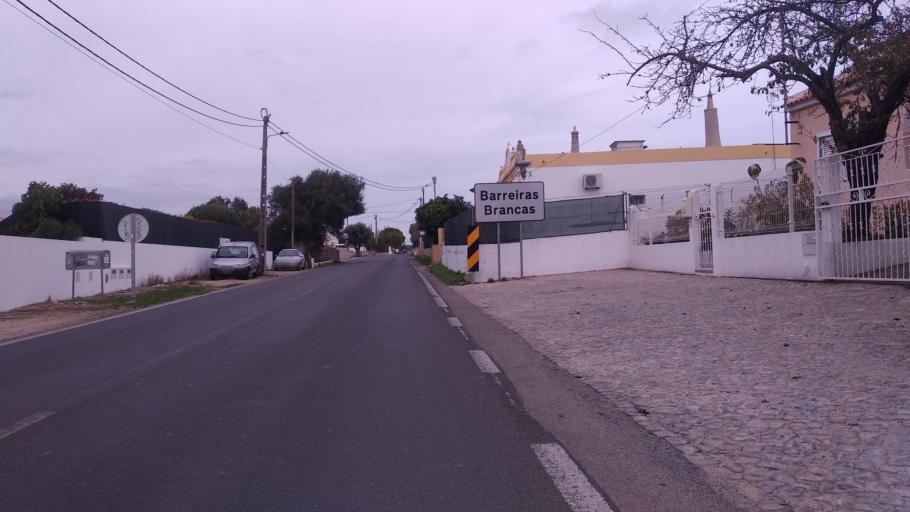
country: PT
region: Faro
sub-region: Loule
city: Loule
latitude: 37.1404
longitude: -7.9850
